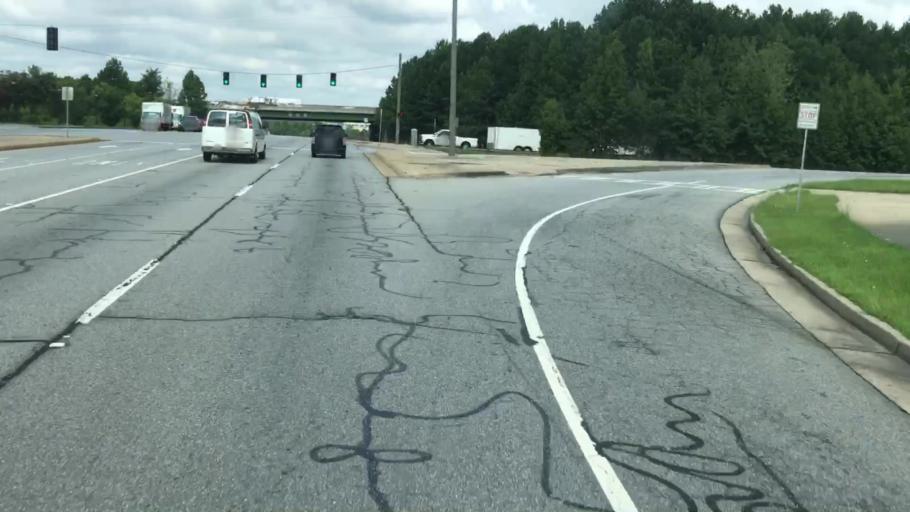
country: US
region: Georgia
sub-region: Gwinnett County
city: Suwanee
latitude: 33.9868
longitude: -84.0812
